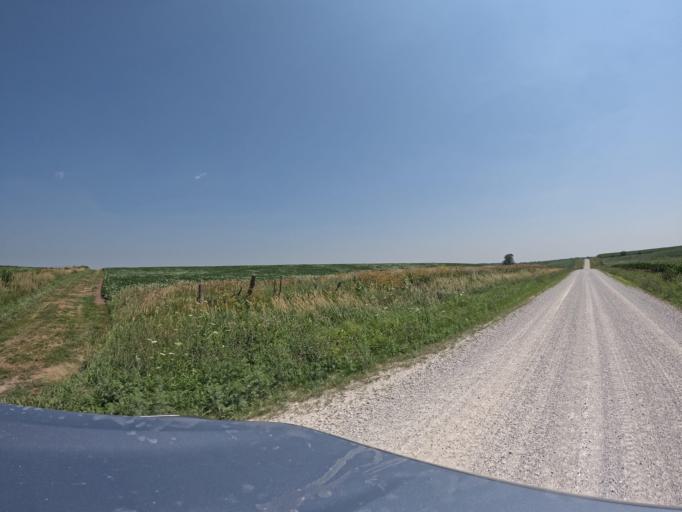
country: US
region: Iowa
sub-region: Keokuk County
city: Sigourney
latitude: 41.3335
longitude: -92.2384
